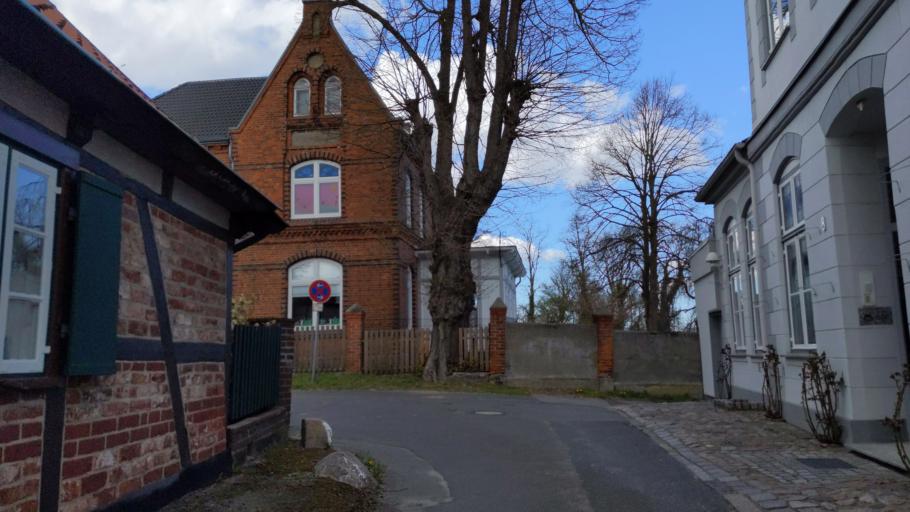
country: DE
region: Mecklenburg-Vorpommern
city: Selmsdorf
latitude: 53.8885
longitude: 10.8005
